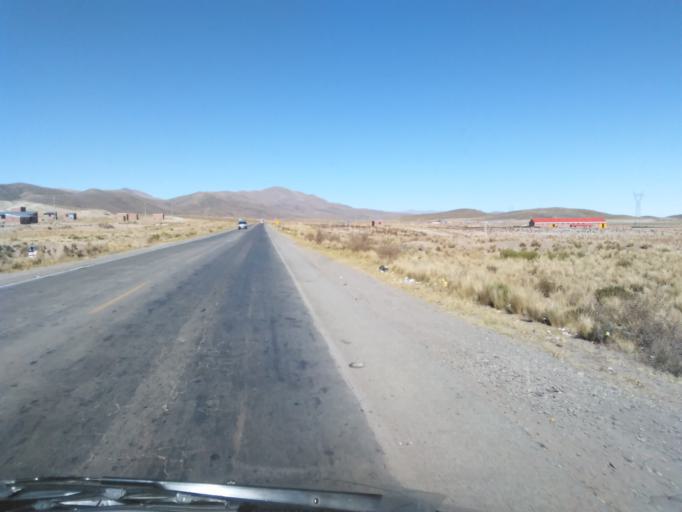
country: BO
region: Oruro
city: Oruro
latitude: -18.0273
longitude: -67.0236
